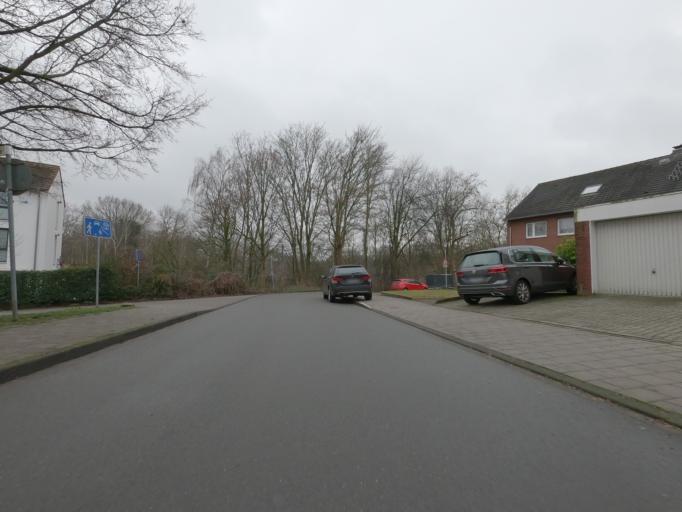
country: DE
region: North Rhine-Westphalia
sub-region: Regierungsbezirk Munster
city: Muenster
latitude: 51.9317
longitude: 7.6204
